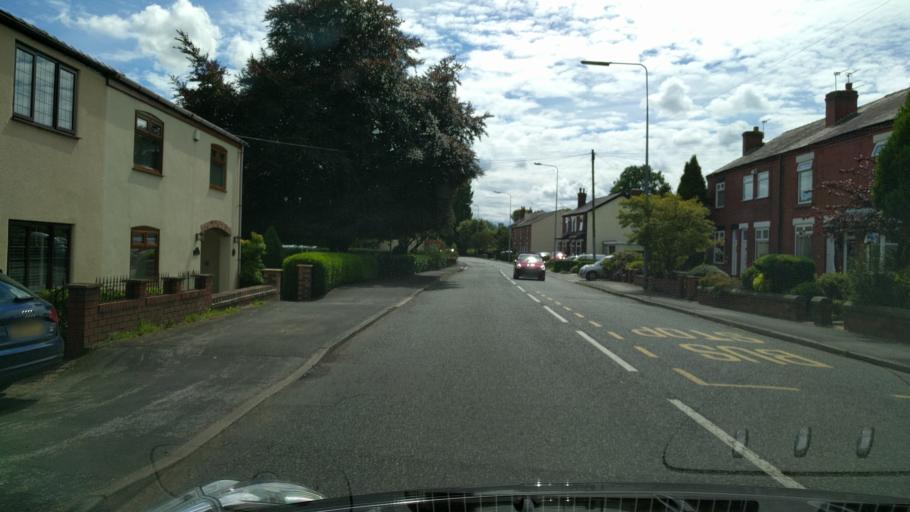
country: GB
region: England
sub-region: Borough of Wigan
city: Leigh
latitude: 53.4666
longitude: -2.4932
